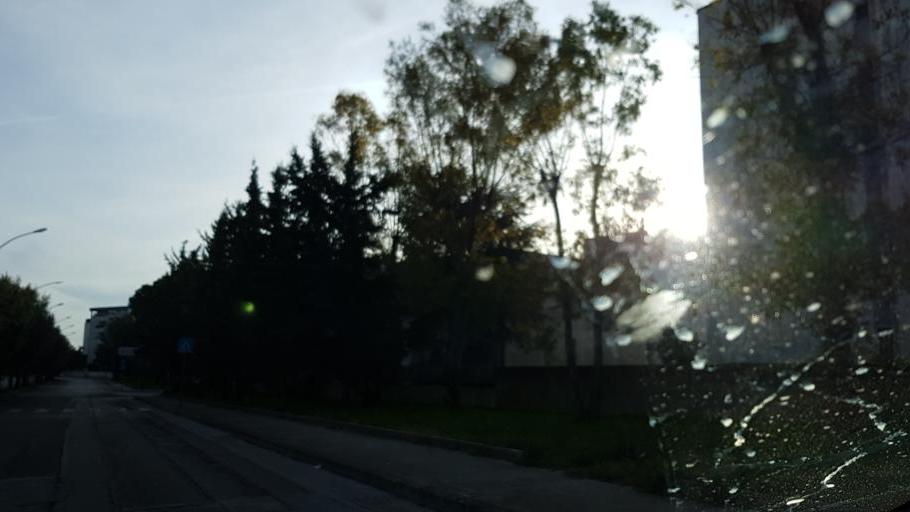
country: IT
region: Apulia
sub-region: Provincia di Brindisi
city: Brindisi
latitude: 40.6256
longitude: 17.9427
